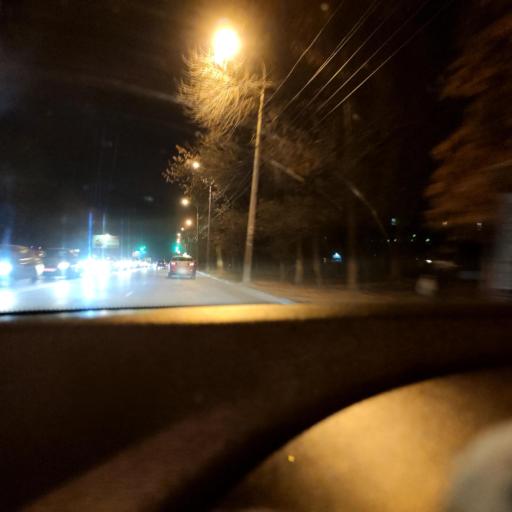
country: RU
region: Samara
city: Samara
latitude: 53.2196
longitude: 50.2052
